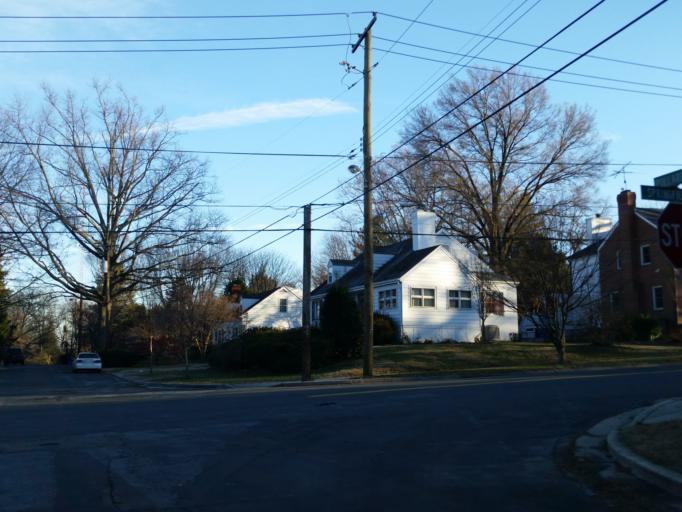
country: US
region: Maryland
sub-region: Montgomery County
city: Somerset
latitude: 38.9685
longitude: -77.1135
